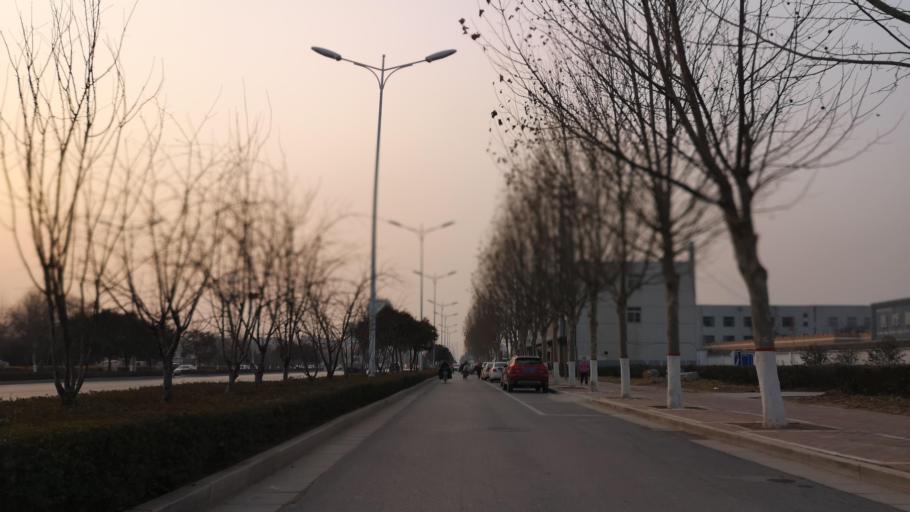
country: CN
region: Henan Sheng
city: Zhongyuanlu
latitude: 35.7889
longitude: 115.0936
